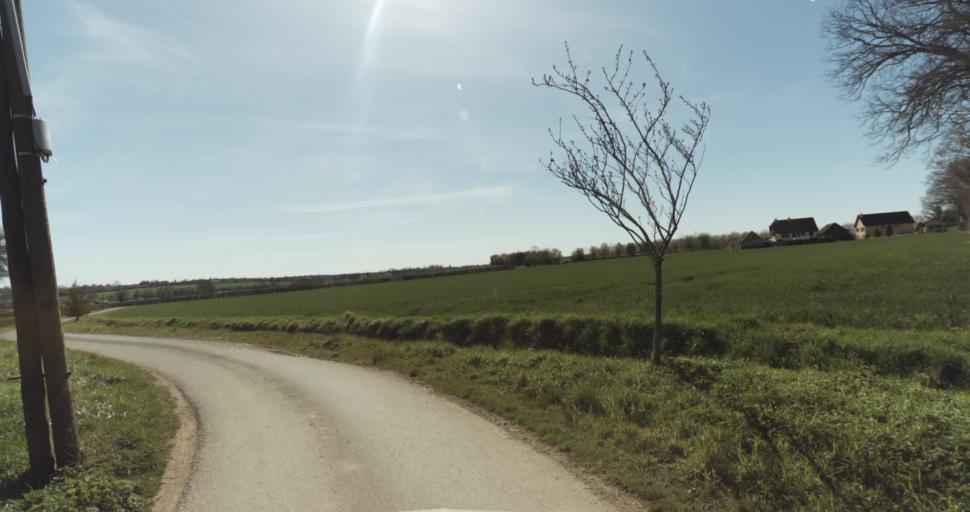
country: FR
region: Lower Normandy
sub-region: Departement du Calvados
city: Saint-Pierre-sur-Dives
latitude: 49.0505
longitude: -0.0160
